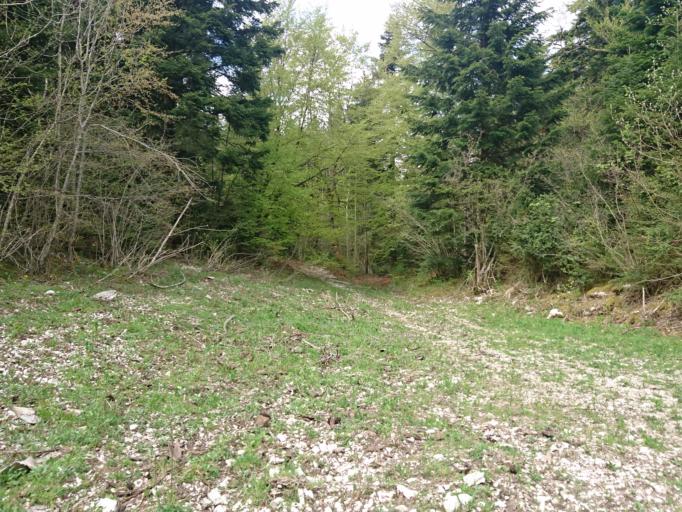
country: FR
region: Rhone-Alpes
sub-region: Departement de l'Ain
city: Nantua
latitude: 46.1645
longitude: 5.6499
